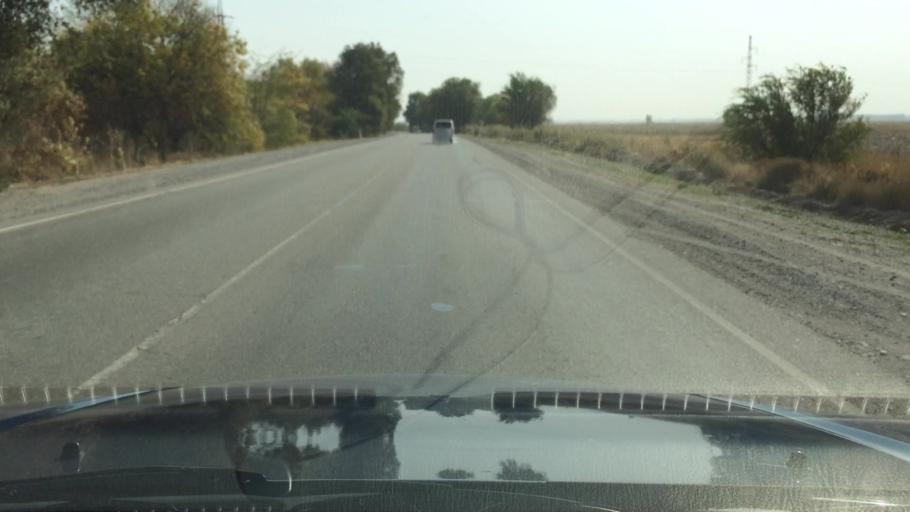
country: KG
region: Chuy
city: Lebedinovka
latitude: 42.9233
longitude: 74.7046
